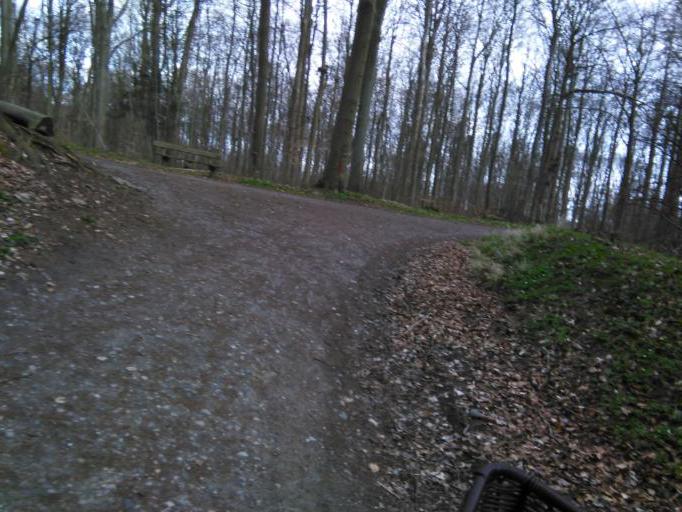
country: DK
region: Central Jutland
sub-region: Arhus Kommune
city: Beder
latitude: 56.1044
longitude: 10.2279
